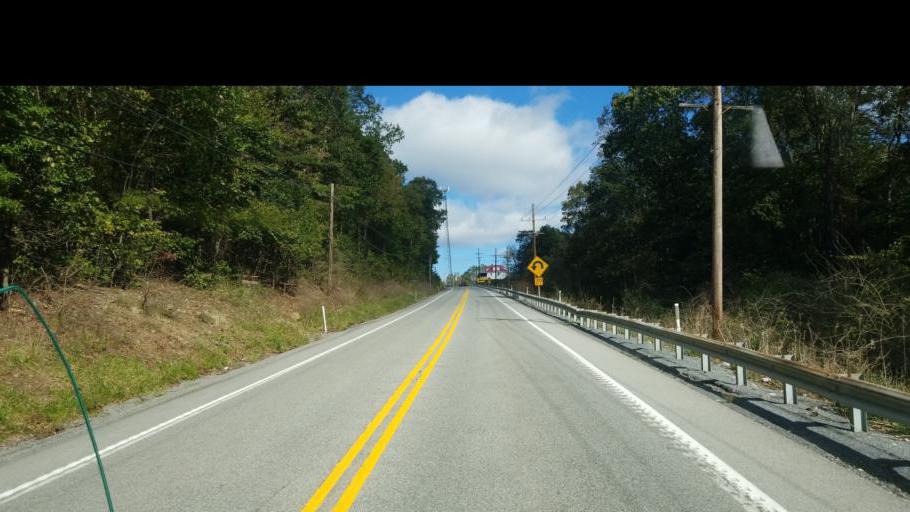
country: US
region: Pennsylvania
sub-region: Fulton County
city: McConnellsburg
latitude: 39.9657
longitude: -78.0243
